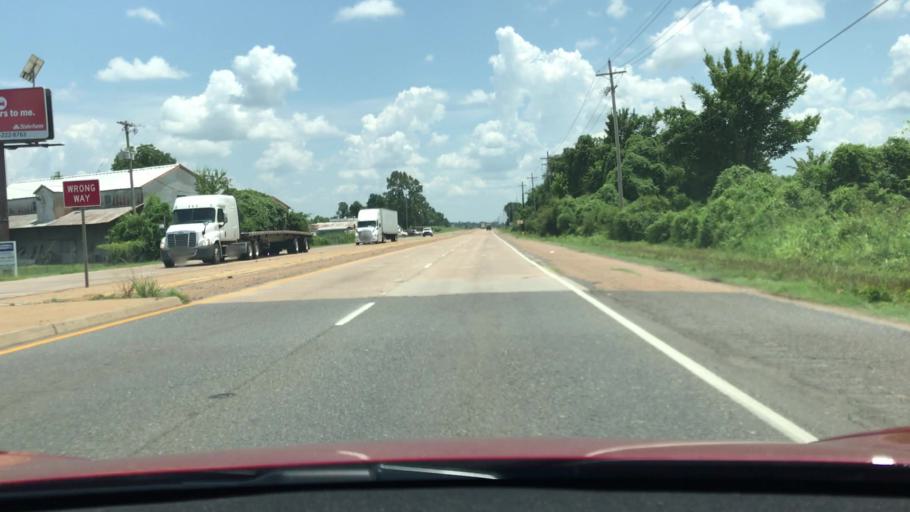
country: US
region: Louisiana
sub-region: Bossier Parish
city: Bossier City
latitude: 32.4002
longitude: -93.6929
